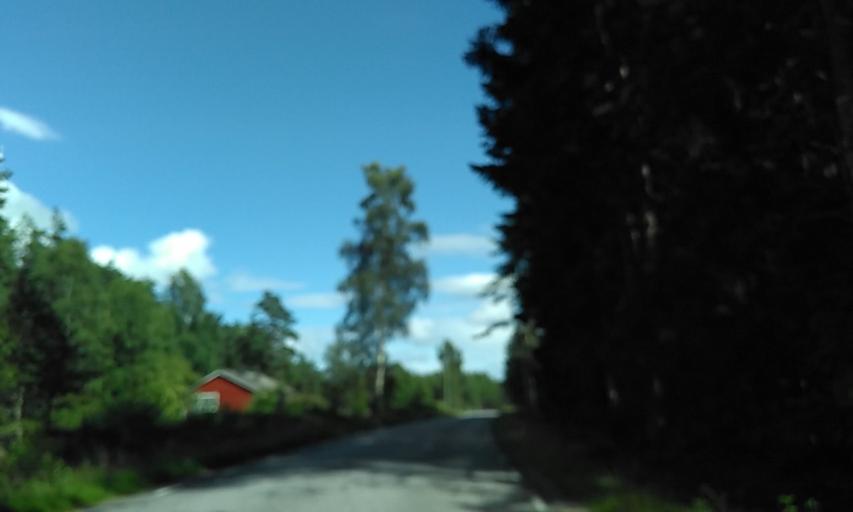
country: SE
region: Vaestra Goetaland
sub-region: Vargarda Kommun
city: Vargarda
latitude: 57.9411
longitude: 12.8107
